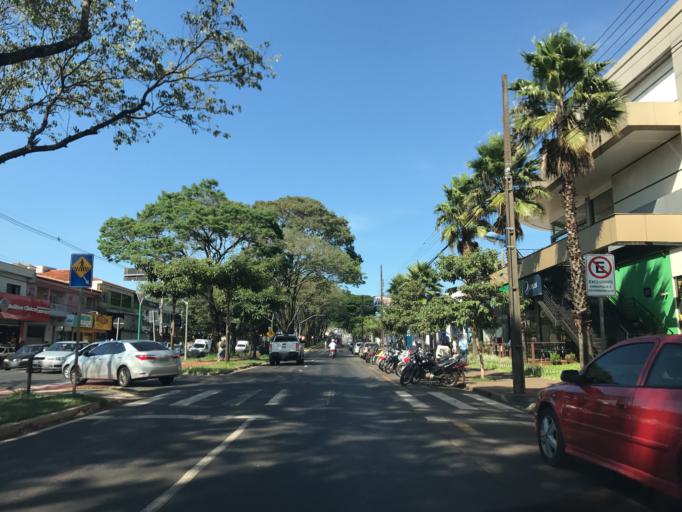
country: BR
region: Parana
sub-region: Maringa
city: Maringa
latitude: -23.4131
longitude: -51.9552
